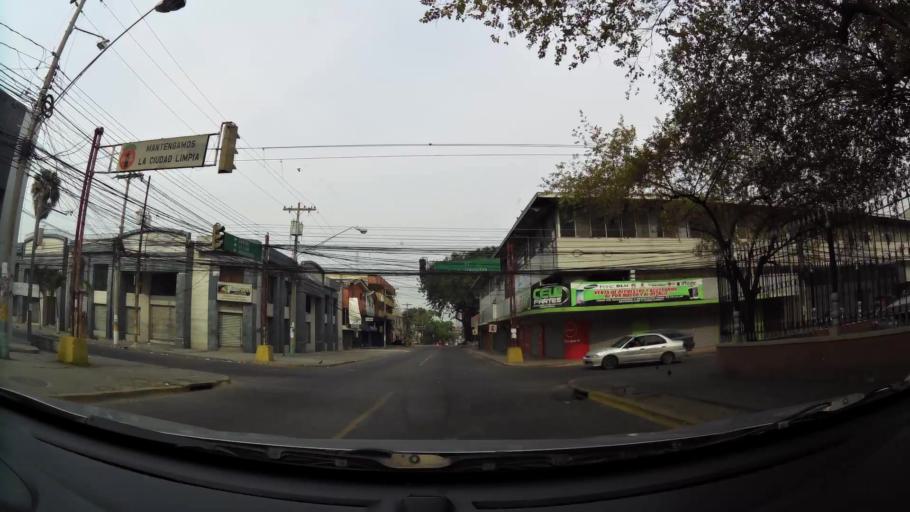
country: HN
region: Cortes
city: San Pedro Sula
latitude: 15.5056
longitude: -88.0237
